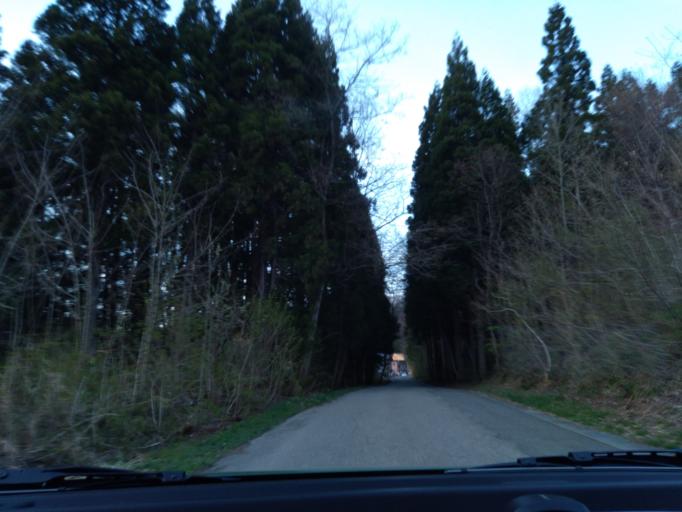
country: JP
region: Akita
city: Kakunodatemachi
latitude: 39.5910
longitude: 140.5779
